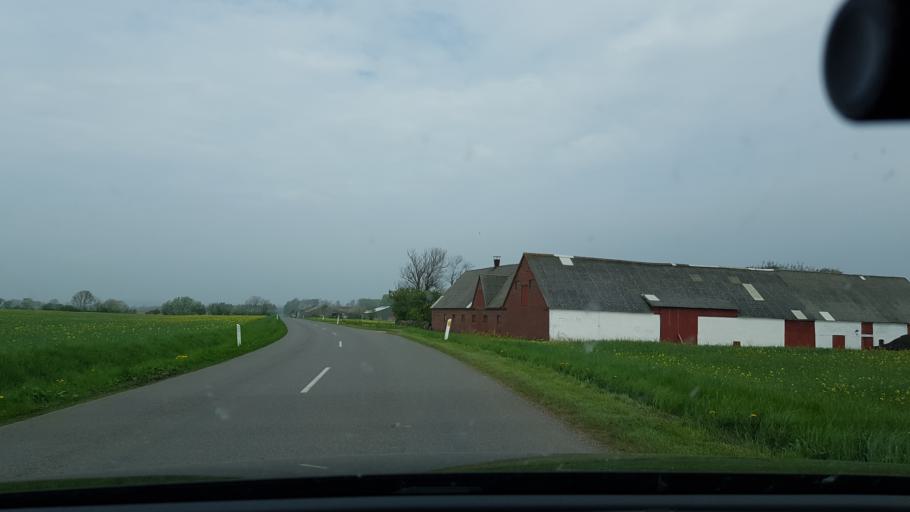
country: DK
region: Capital Region
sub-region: Bornholm Kommune
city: Nexo
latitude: 55.0106
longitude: 15.0956
